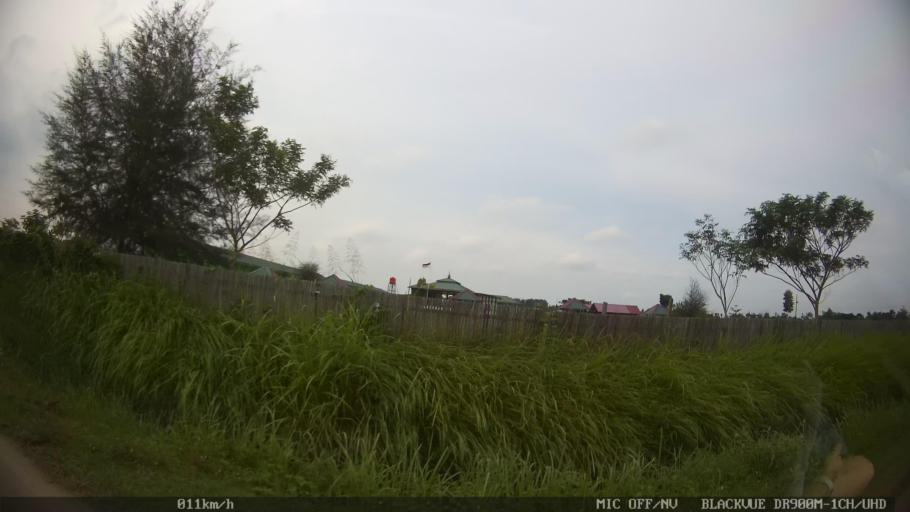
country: ID
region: North Sumatra
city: Medan
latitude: 3.5734
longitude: 98.7428
